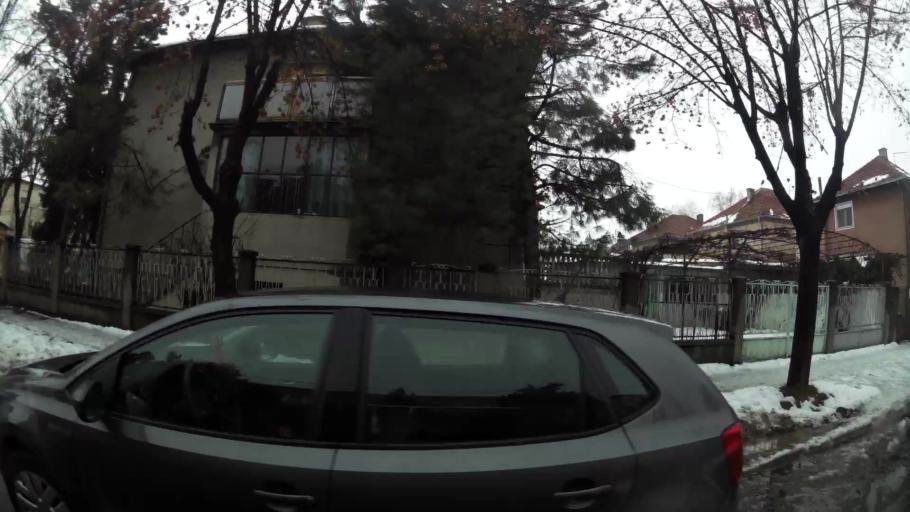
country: RS
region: Central Serbia
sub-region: Belgrade
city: Zemun
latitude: 44.8402
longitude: 20.3721
